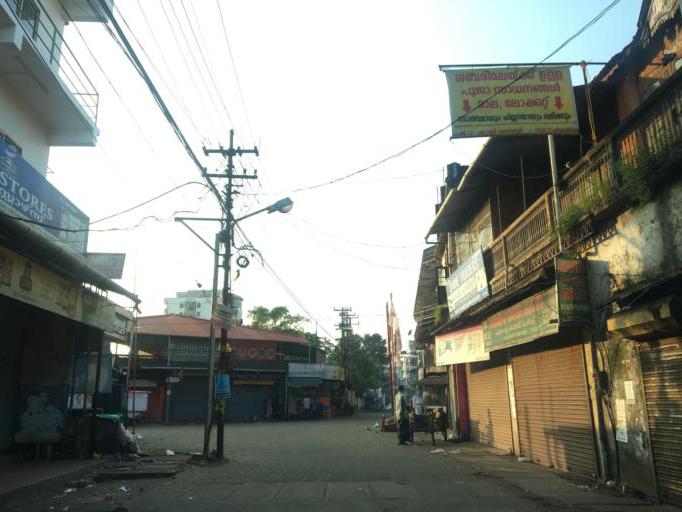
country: IN
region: Kerala
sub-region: Ernakulam
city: Cochin
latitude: 9.9809
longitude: 76.2783
